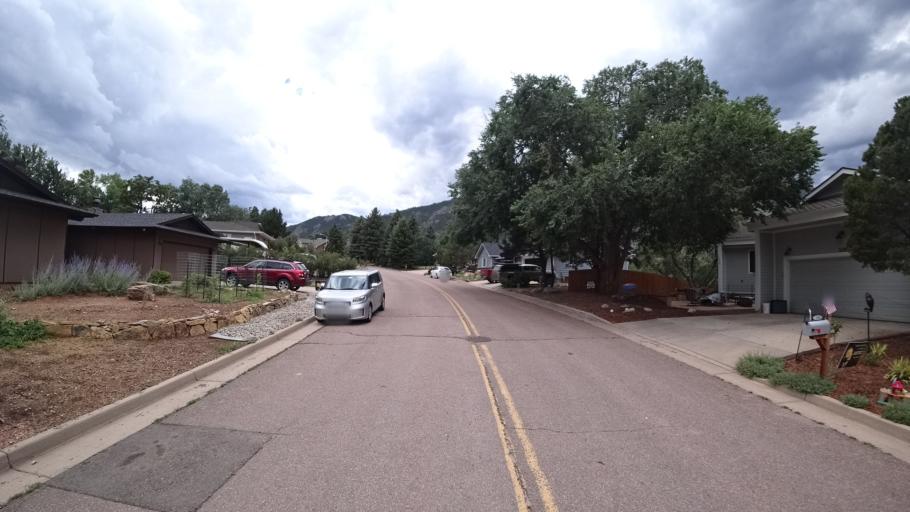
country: US
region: Colorado
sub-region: El Paso County
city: Manitou Springs
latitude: 38.8472
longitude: -104.8948
